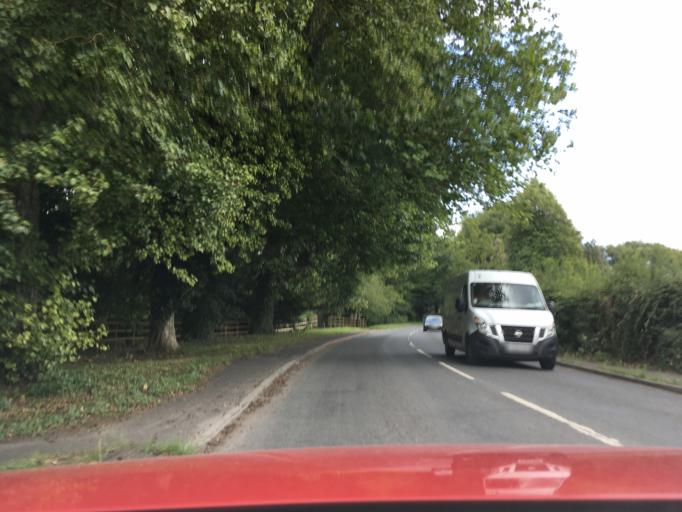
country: GB
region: England
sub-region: Hampshire
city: Kings Worthy
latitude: 51.0884
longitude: -1.3070
